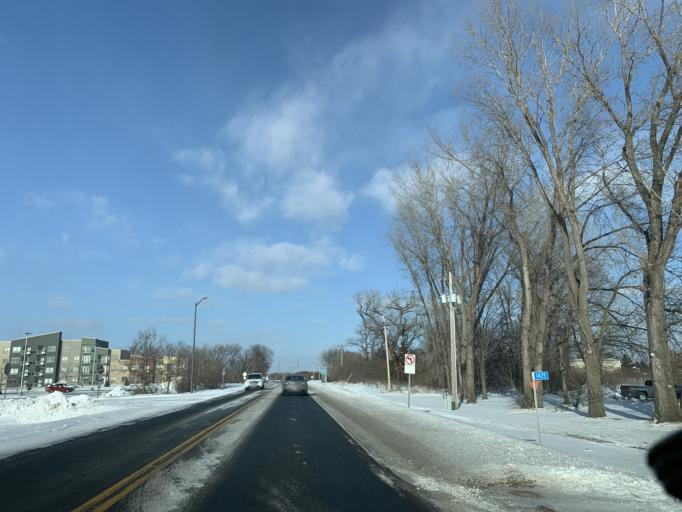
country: US
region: Minnesota
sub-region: Scott County
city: Prior Lake
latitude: 44.7790
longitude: -93.4064
